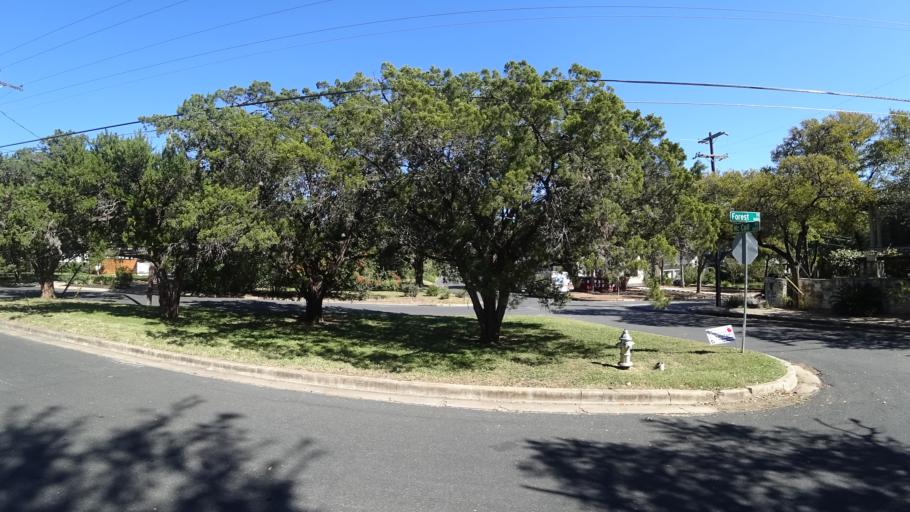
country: US
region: Texas
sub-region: Travis County
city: Rollingwood
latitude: 30.2902
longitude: -97.7662
